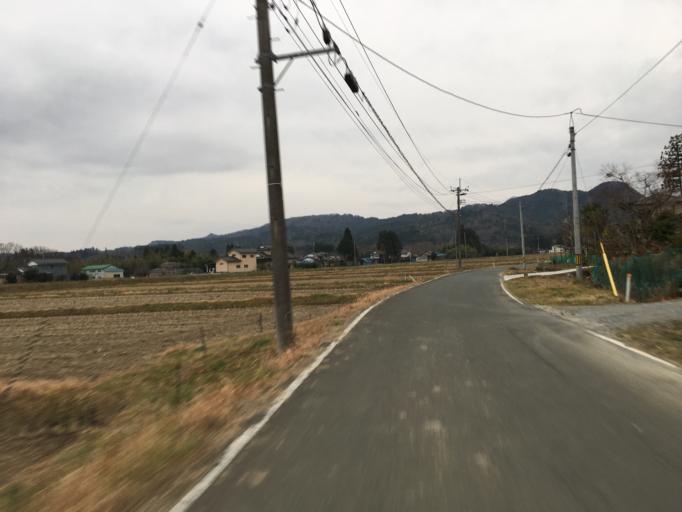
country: JP
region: Miyagi
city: Marumori
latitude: 37.7801
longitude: 140.8953
